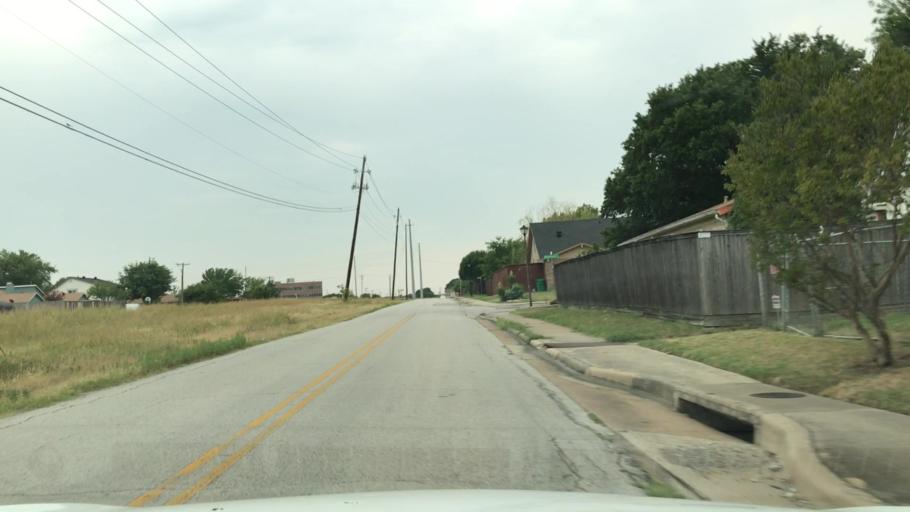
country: US
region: Texas
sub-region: Dallas County
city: Carrollton
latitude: 32.9891
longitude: -96.8753
